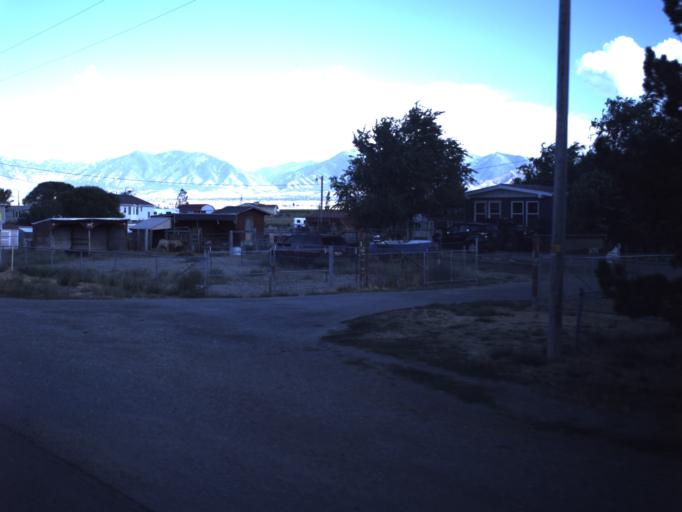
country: US
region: Utah
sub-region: Tooele County
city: Grantsville
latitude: 40.5995
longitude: -112.4173
